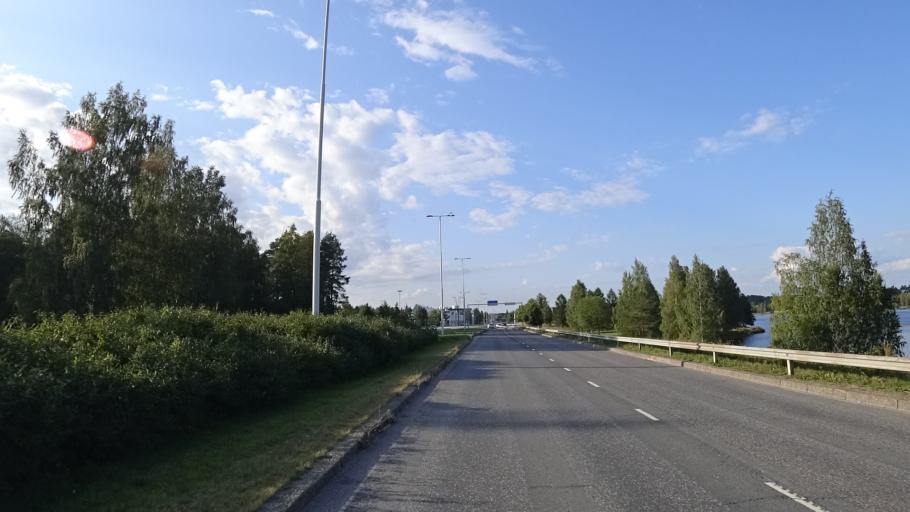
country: FI
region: South Karelia
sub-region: Imatra
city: Imatra
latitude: 61.1871
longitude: 28.7779
